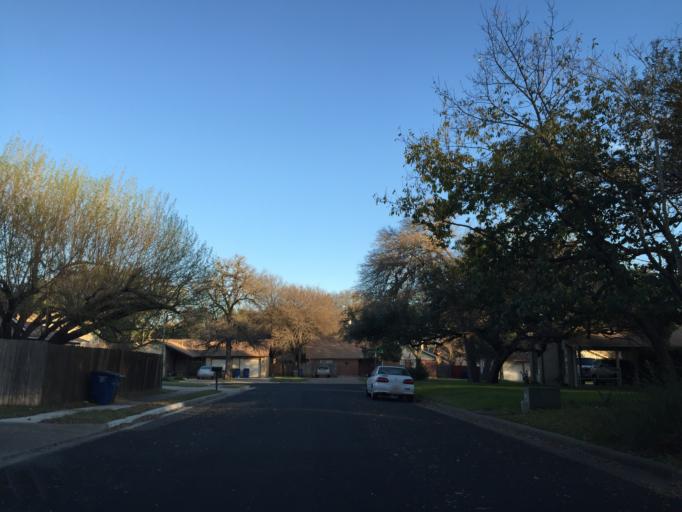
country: US
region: Texas
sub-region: Williamson County
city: Jollyville
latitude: 30.4274
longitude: -97.7638
